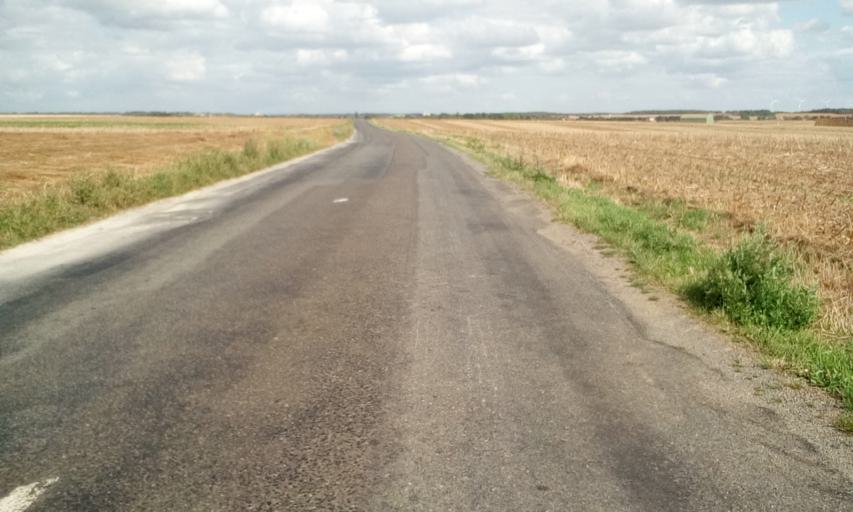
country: FR
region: Lower Normandy
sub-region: Departement du Calvados
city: Bellengreville
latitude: 49.0917
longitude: -0.2229
